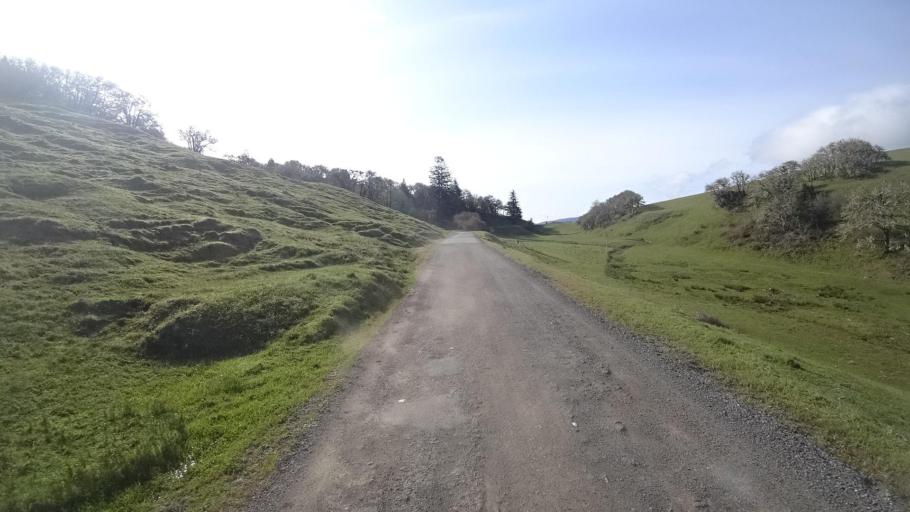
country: US
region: California
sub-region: Humboldt County
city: Hydesville
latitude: 40.6465
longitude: -123.9220
